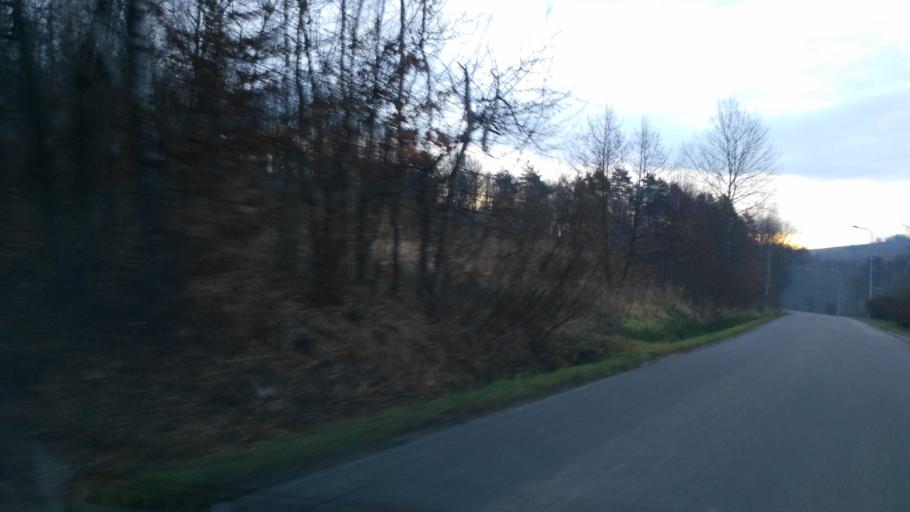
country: PL
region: Subcarpathian Voivodeship
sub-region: Powiat strzyzowski
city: Niebylec
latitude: 49.8599
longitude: 21.8936
